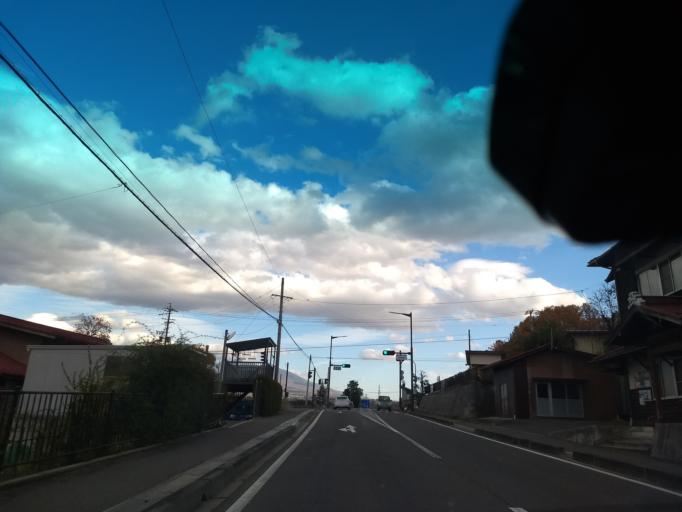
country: JP
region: Nagano
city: Chino
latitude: 35.9961
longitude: 138.1290
